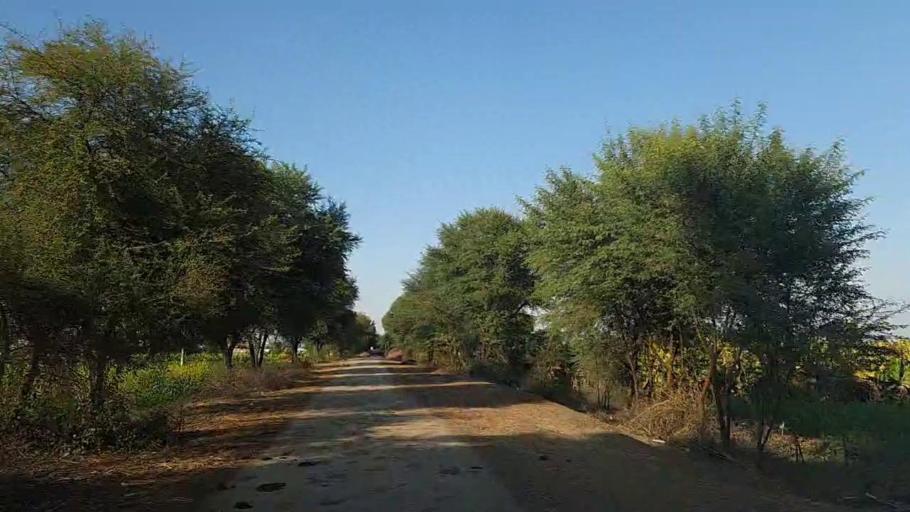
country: PK
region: Sindh
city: Shahpur Chakar
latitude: 26.1953
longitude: 68.6336
